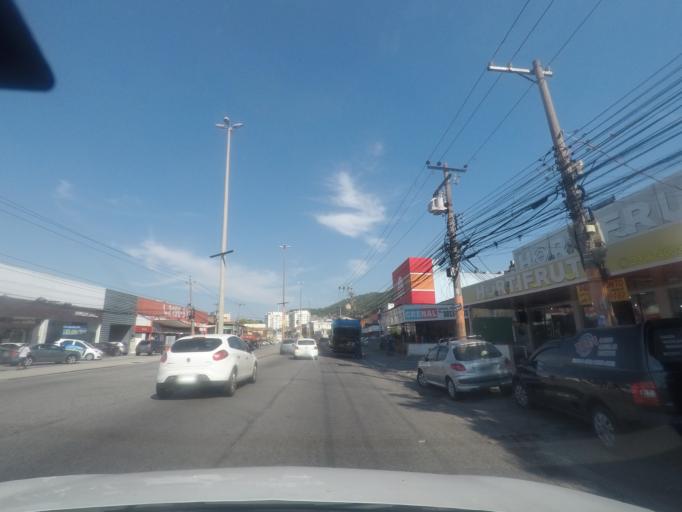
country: BR
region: Rio de Janeiro
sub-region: Sao Joao De Meriti
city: Sao Joao de Meriti
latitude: -22.8820
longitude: -43.3500
